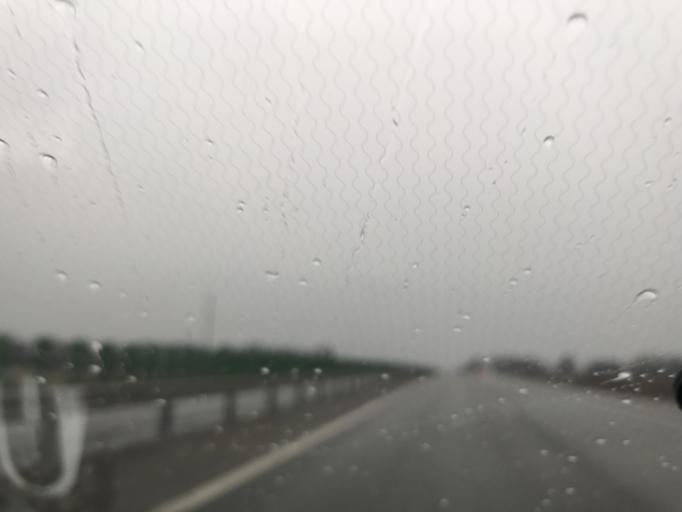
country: RU
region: Krasnodarskiy
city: Kislyakovskaya
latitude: 46.3445
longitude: 39.7772
